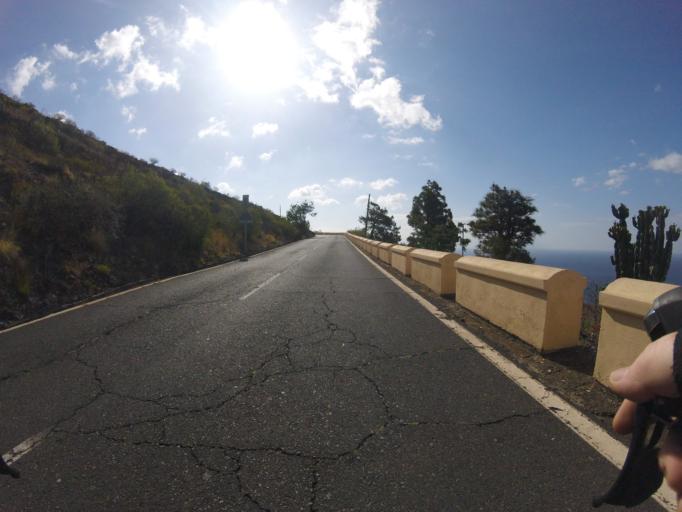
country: ES
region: Canary Islands
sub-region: Provincia de Santa Cruz de Tenerife
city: Candelaria
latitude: 28.4076
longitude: -16.3389
